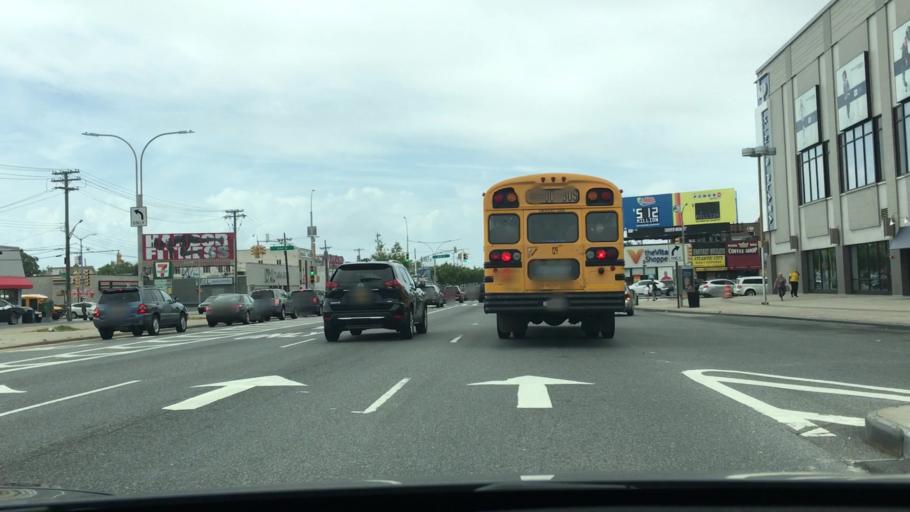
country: US
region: New York
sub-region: Kings County
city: Brooklyn
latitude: 40.6093
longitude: -73.9217
